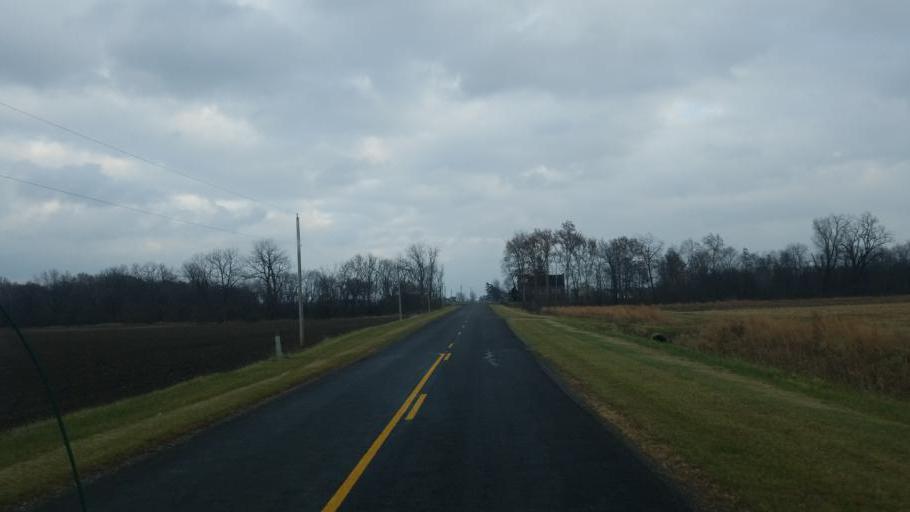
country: US
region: Ohio
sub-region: Mercer County
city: Fort Recovery
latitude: 40.5090
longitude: -84.7459
